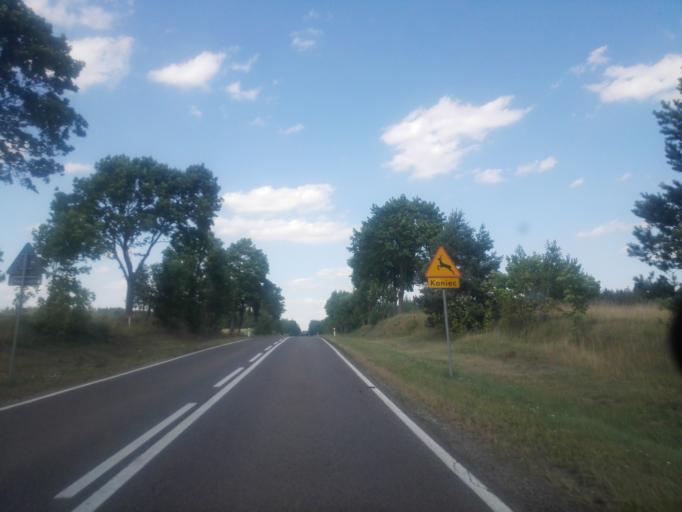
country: PL
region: Podlasie
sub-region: Powiat sejnenski
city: Sejny
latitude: 54.0238
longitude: 23.3433
